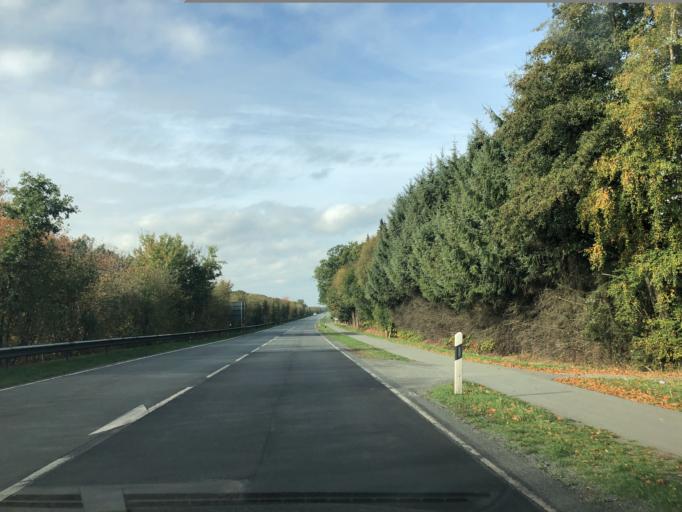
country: DE
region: Lower Saxony
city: Edewecht
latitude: 53.0878
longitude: 7.9375
